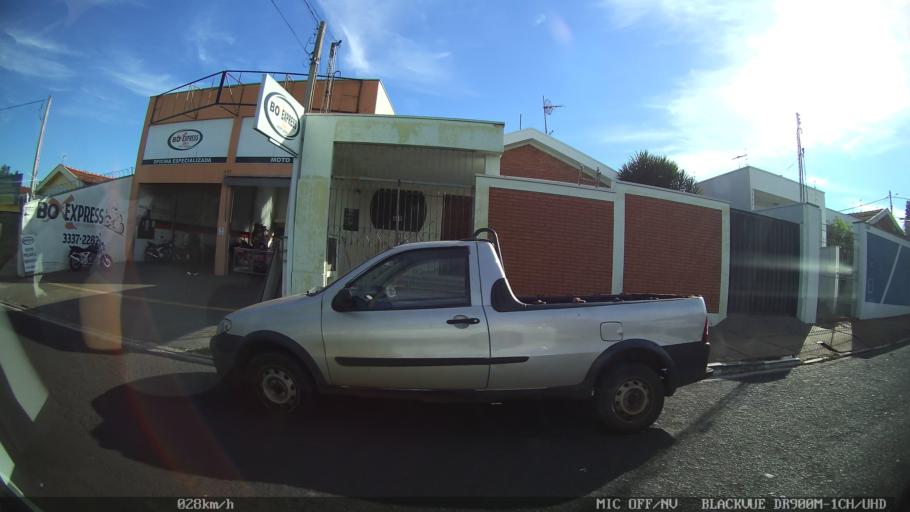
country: BR
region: Sao Paulo
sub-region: Araraquara
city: Araraquara
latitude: -21.7899
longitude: -48.1573
